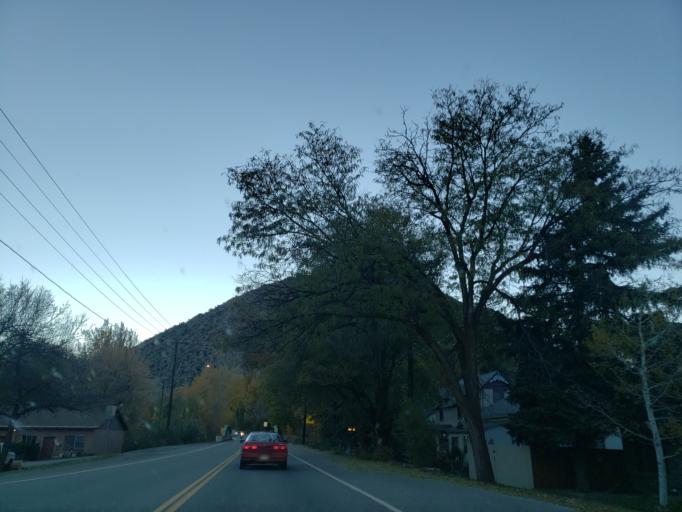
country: US
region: Colorado
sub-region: Garfield County
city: New Castle
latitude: 39.5715
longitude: -107.5382
